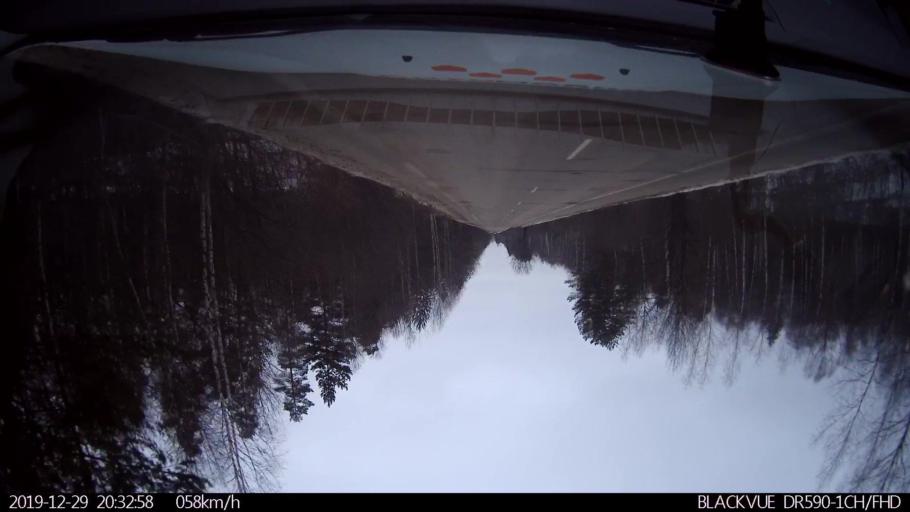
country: RU
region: Nizjnij Novgorod
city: Afonino
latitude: 56.1780
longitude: 44.0575
